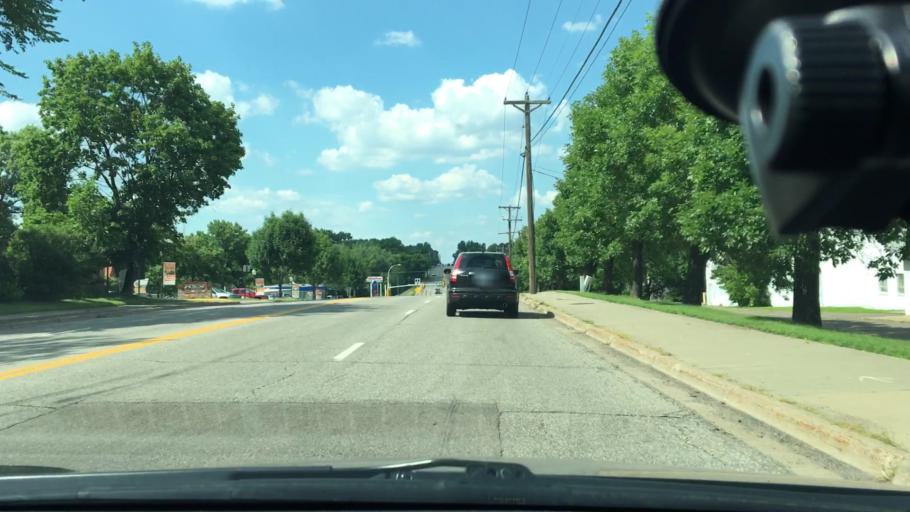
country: US
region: Minnesota
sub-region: Hennepin County
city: New Hope
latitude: 45.0198
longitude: -93.3802
